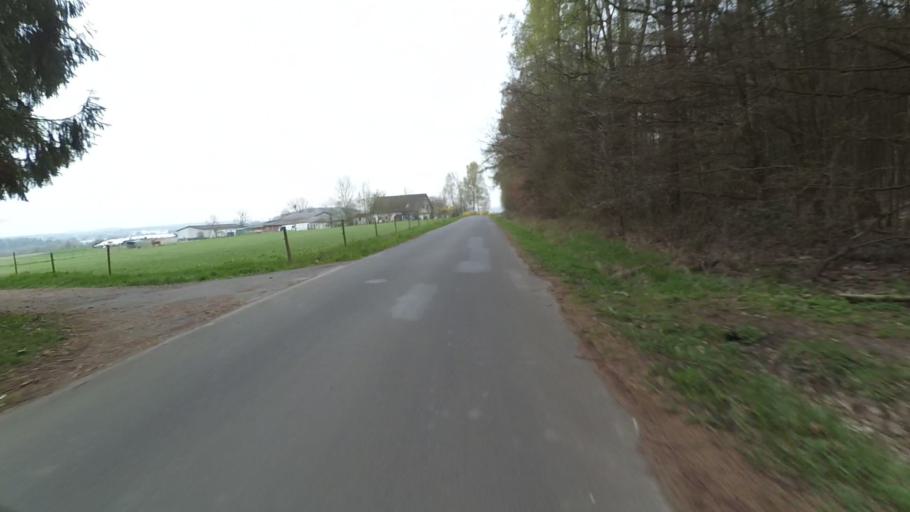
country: DE
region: Rheinland-Pfalz
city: Bannberscheid
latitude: 50.4565
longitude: 7.8294
